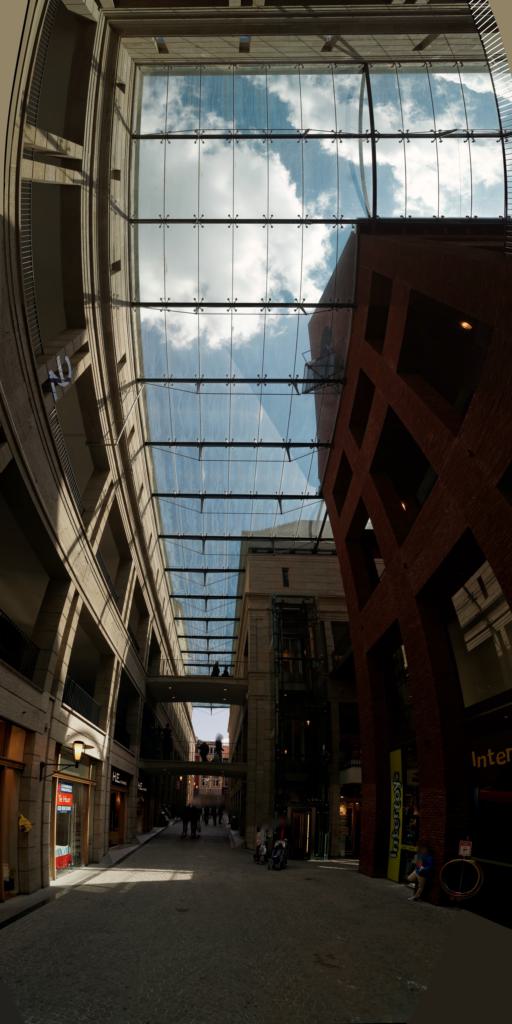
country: NL
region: Limburg
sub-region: Gemeente Maastricht
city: Maastricht
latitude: 50.8505
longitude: 5.6893
